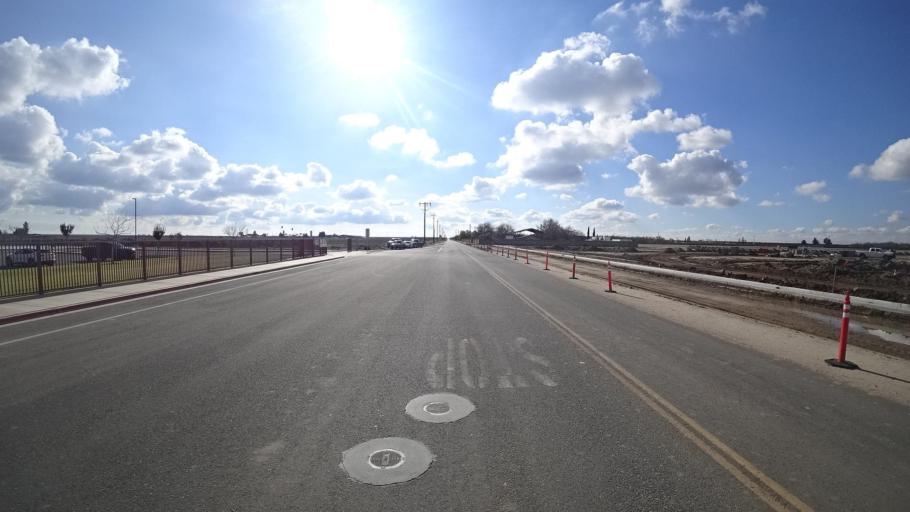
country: US
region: California
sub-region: Kern County
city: McFarland
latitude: 35.6662
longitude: -119.2409
